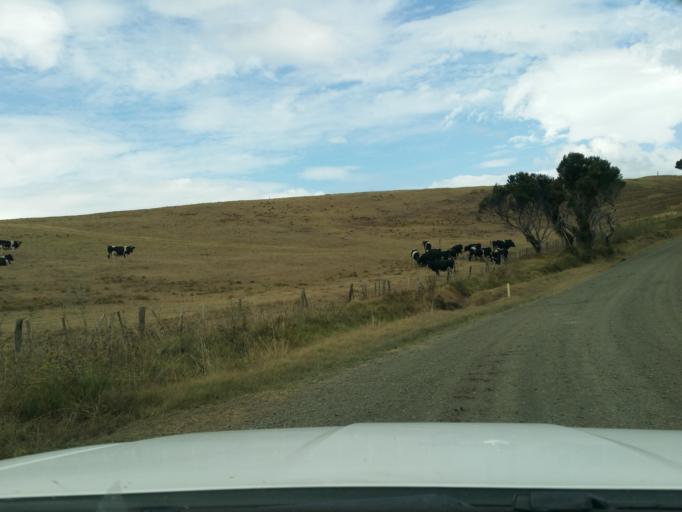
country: NZ
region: Auckland
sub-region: Auckland
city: Wellsford
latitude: -36.3312
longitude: 174.1558
